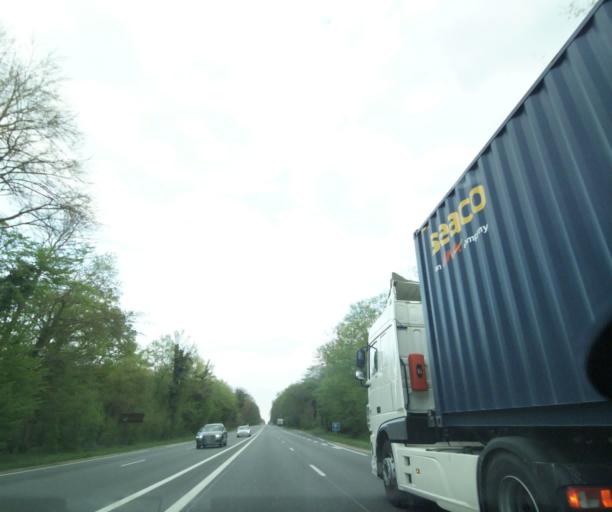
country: FR
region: Ile-de-France
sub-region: Departement de Seine-et-Marne
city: Fontainebleau
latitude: 48.4286
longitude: 2.6630
